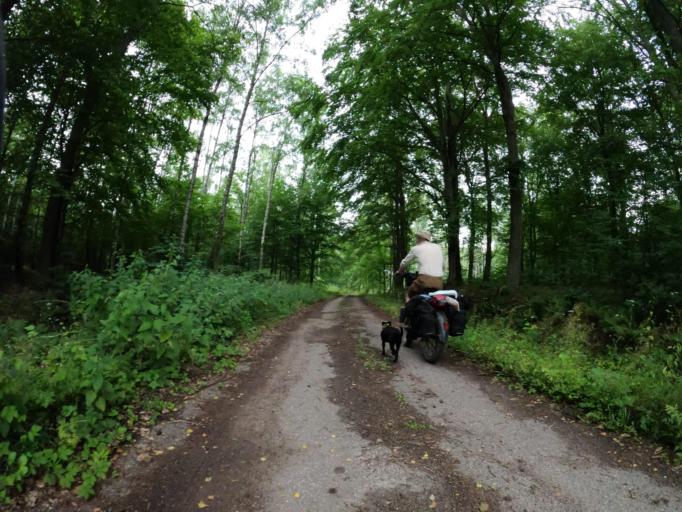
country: PL
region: West Pomeranian Voivodeship
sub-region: Powiat szczecinecki
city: Borne Sulinowo
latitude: 53.7064
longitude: 16.4934
